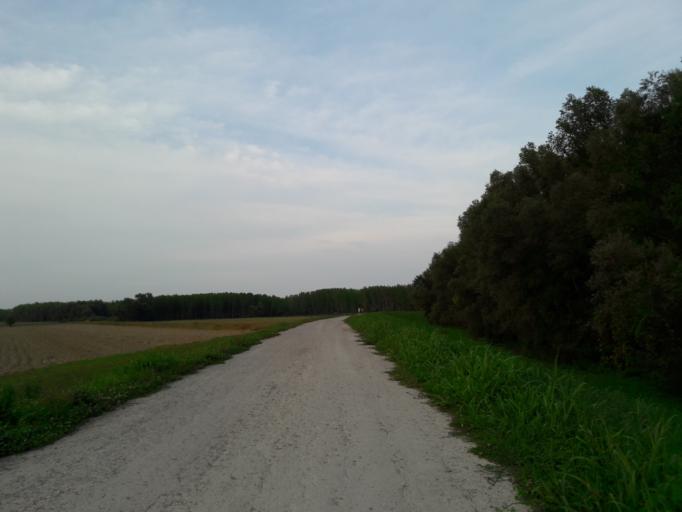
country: HR
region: Osjecko-Baranjska
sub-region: Grad Osijek
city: Osijek
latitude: 45.5652
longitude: 18.7220
